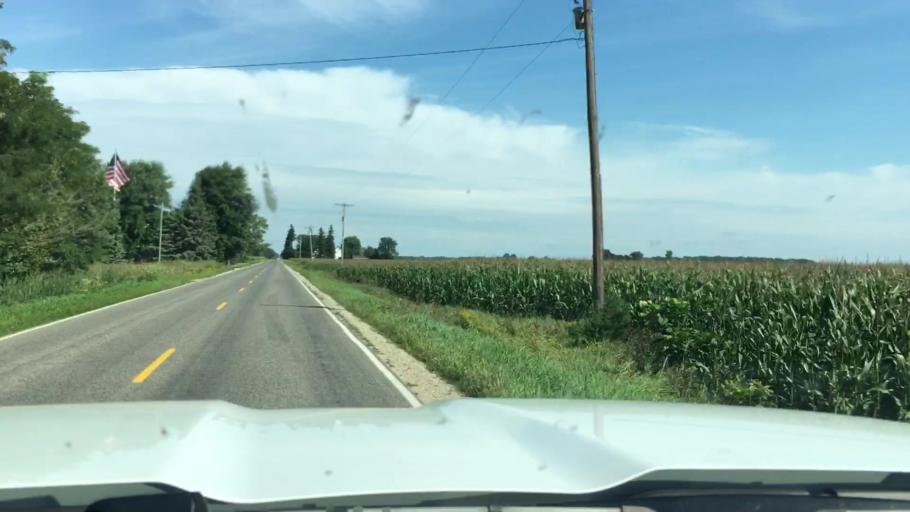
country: US
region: Michigan
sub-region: Saginaw County
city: Hemlock
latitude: 43.5139
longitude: -84.2296
